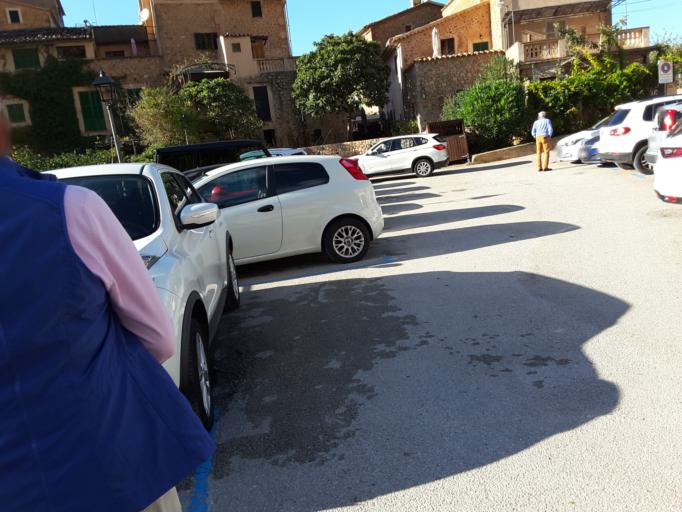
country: ES
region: Balearic Islands
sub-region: Illes Balears
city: Deia
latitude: 39.7484
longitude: 2.6489
